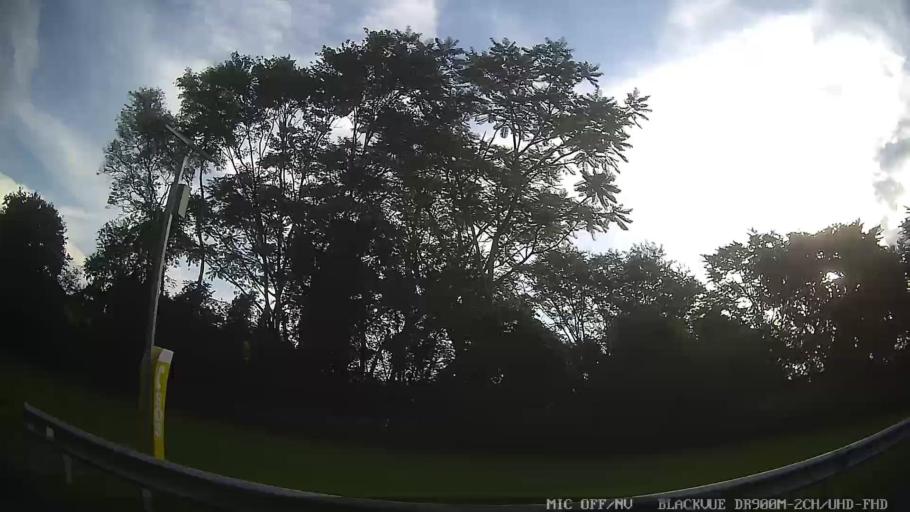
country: BR
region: Sao Paulo
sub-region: Tiete
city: Tiete
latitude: -23.1390
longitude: -47.6809
